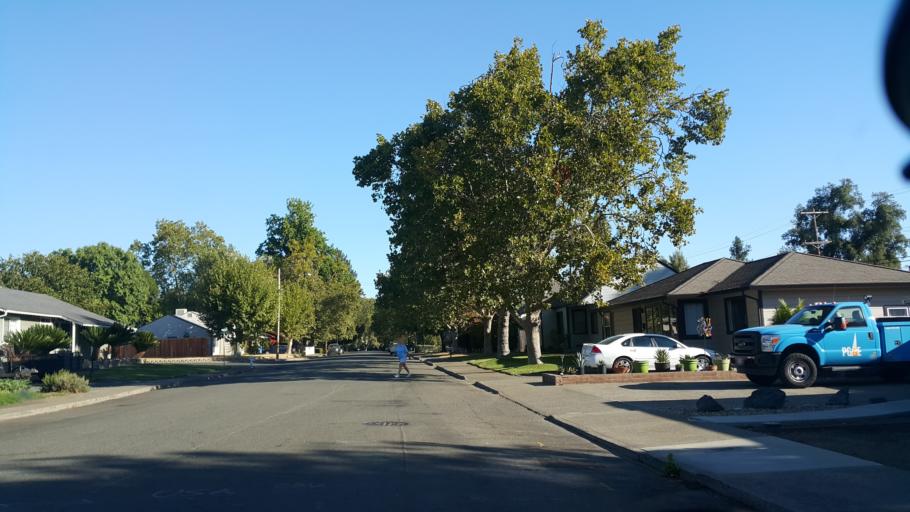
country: US
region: California
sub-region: Mendocino County
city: Ukiah
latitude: 39.1407
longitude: -123.2134
